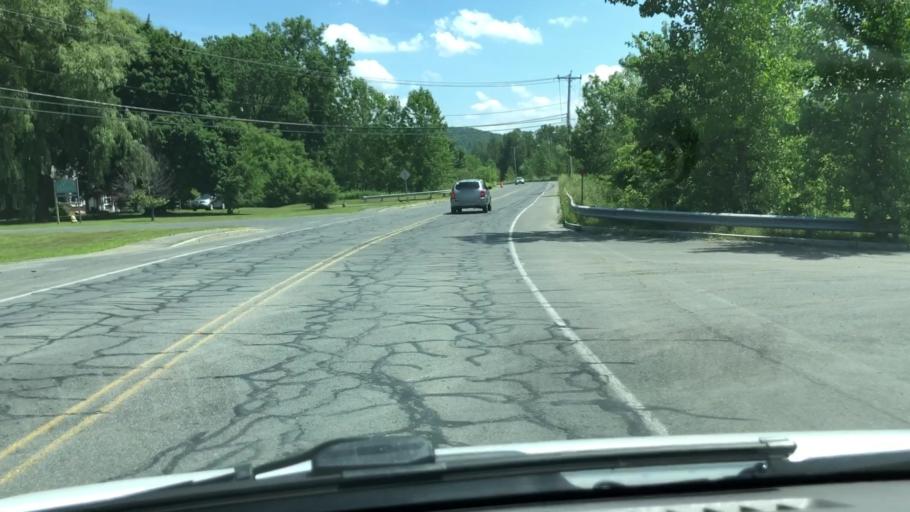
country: US
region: Massachusetts
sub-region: Berkshire County
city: Pittsfield
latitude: 42.4543
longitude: -73.2074
